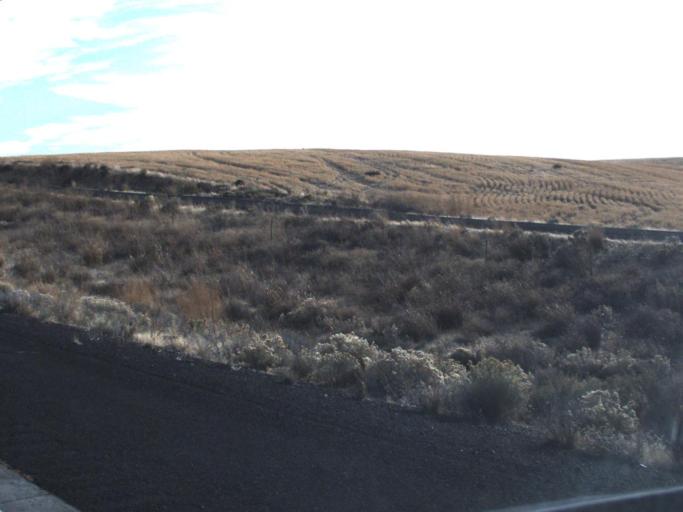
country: US
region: Washington
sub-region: Adams County
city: Ritzville
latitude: 47.0134
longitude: -118.5074
